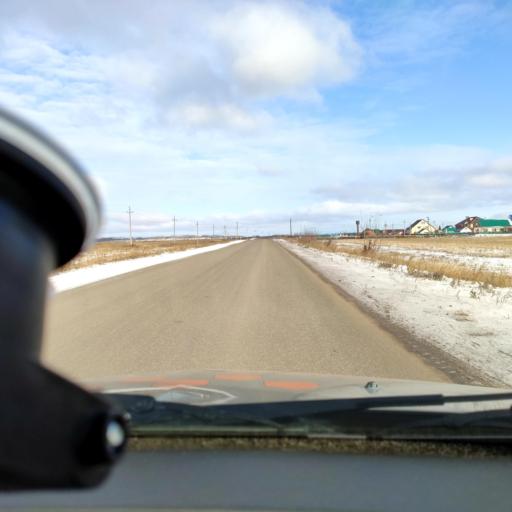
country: RU
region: Bashkortostan
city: Mikhaylovka
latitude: 54.8080
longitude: 55.7825
